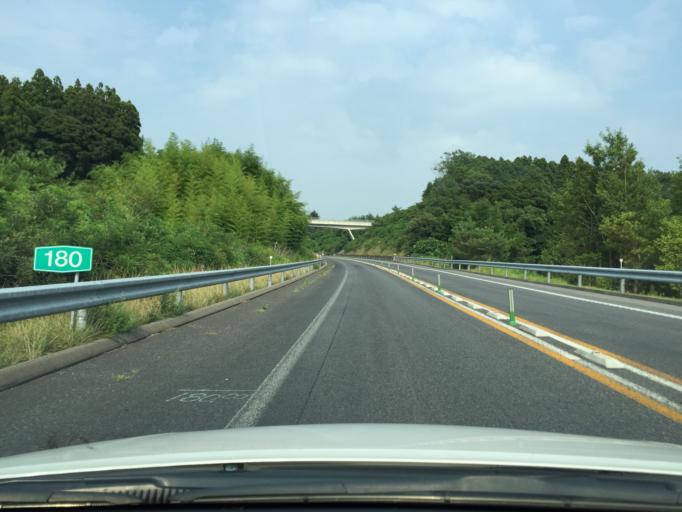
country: JP
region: Fukushima
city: Iwaki
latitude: 37.0966
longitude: 140.8654
